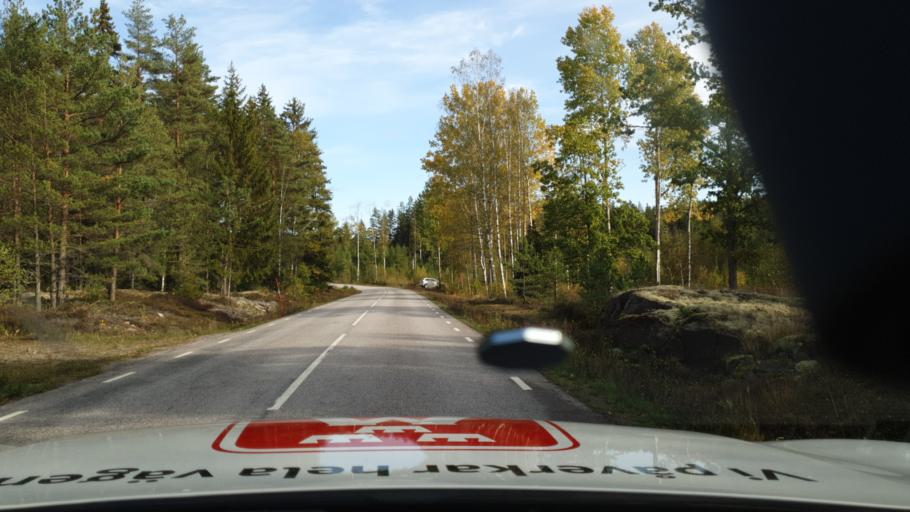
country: SE
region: Kalmar
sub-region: Vasterviks Kommun
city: Overum
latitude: 58.0479
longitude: 16.3315
